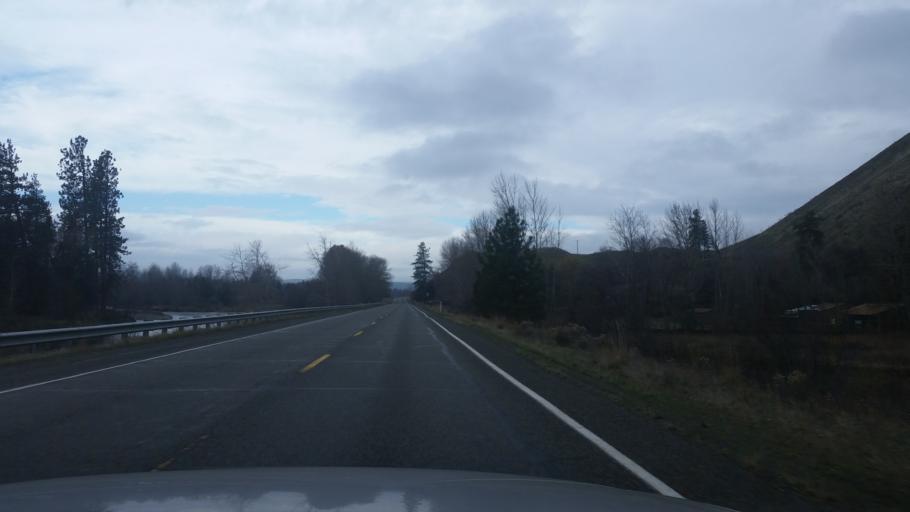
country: US
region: Washington
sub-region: Kittitas County
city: Ellensburg
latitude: 47.0751
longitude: -120.6629
